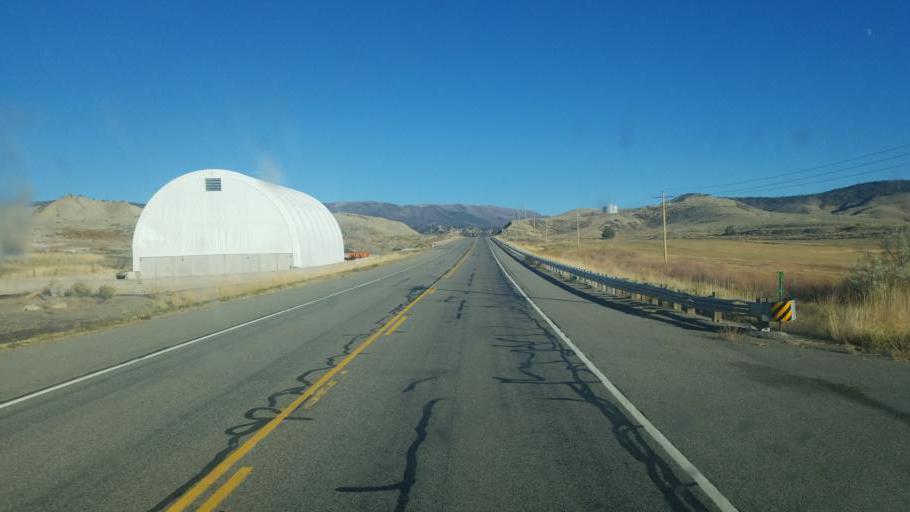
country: US
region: Colorado
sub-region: Montrose County
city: Montrose
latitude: 38.4885
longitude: -107.7649
